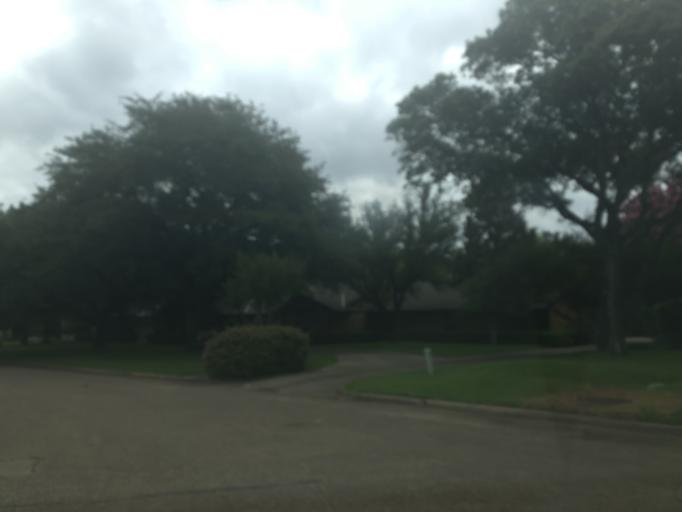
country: US
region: Texas
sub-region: Dallas County
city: University Park
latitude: 32.8843
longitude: -96.8322
